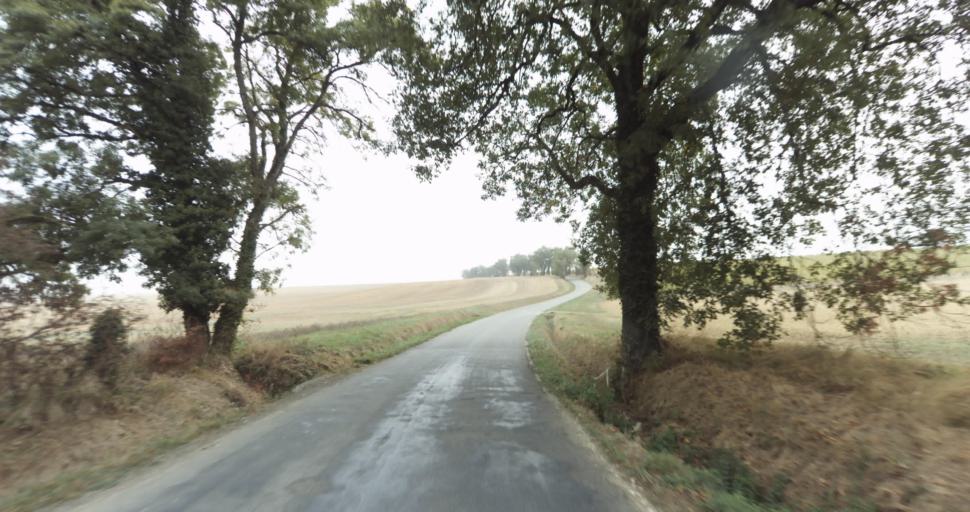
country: FR
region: Midi-Pyrenees
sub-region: Departement du Gers
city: Preignan
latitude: 43.6949
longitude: 0.5899
